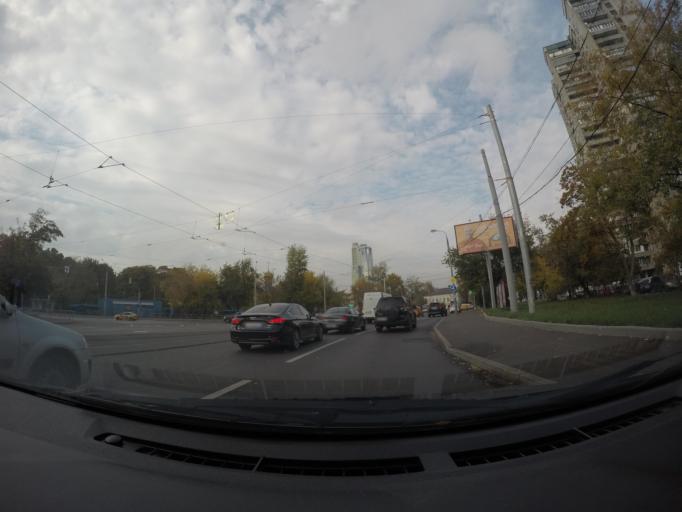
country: RU
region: Moscow
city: Lefortovo
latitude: 55.7783
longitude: 37.7210
